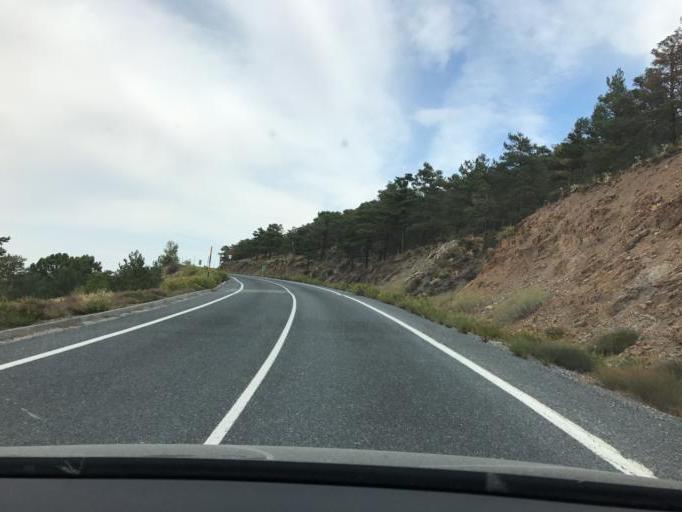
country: ES
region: Andalusia
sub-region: Provincia de Granada
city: Aldeire
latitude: 37.1450
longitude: -3.0484
